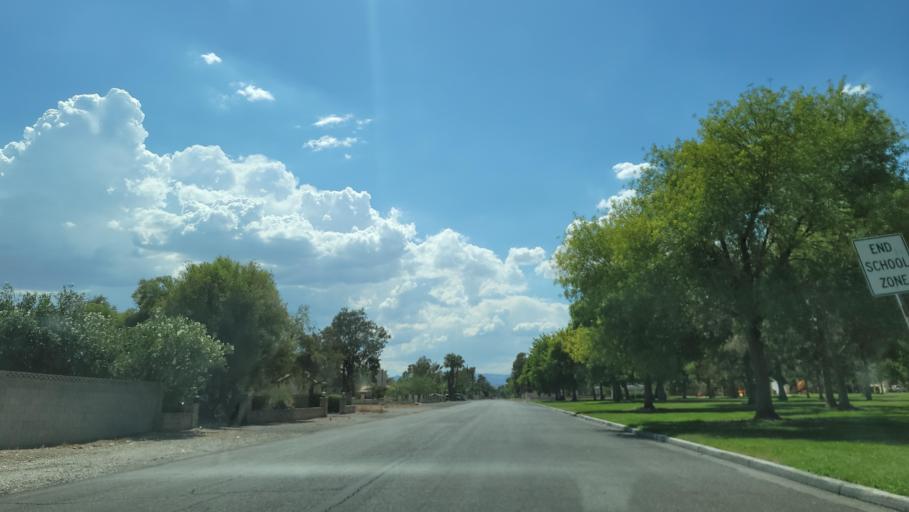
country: US
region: Nevada
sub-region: Clark County
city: Spring Valley
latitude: 36.1386
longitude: -115.2366
